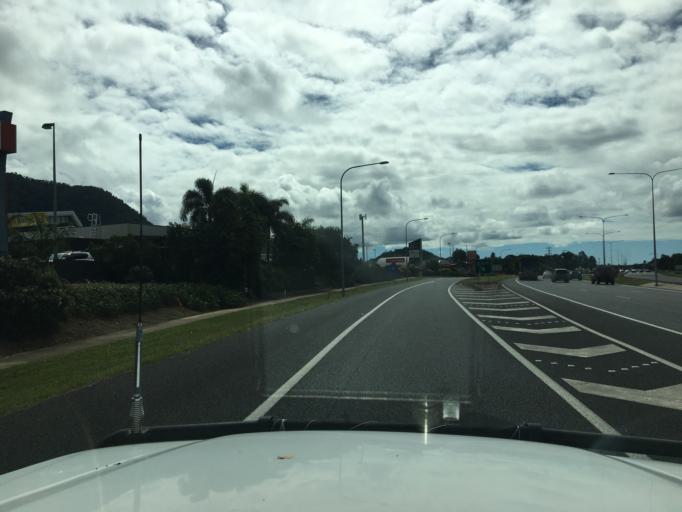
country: AU
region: Queensland
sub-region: Cairns
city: Woree
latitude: -16.9909
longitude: 145.7414
